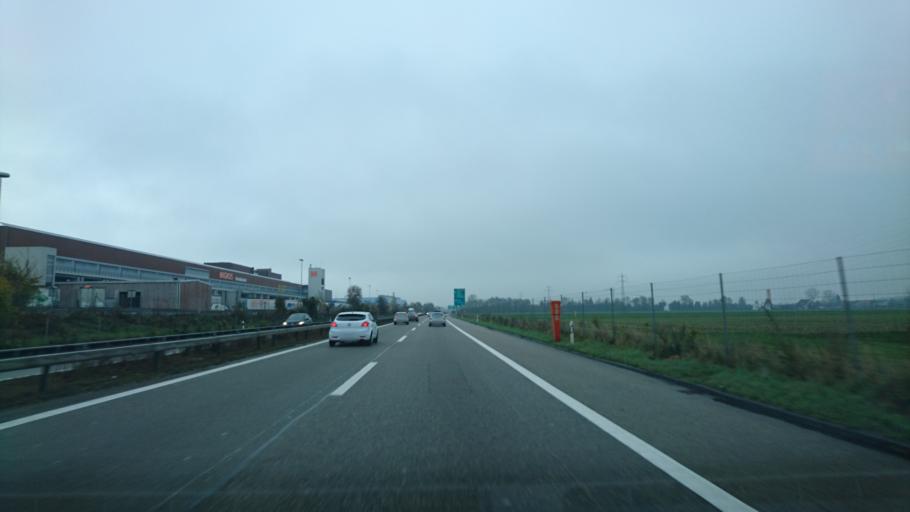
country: CH
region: Solothurn
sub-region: Bezirk Gaeu
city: Egerkingen
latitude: 47.3058
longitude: 7.7805
